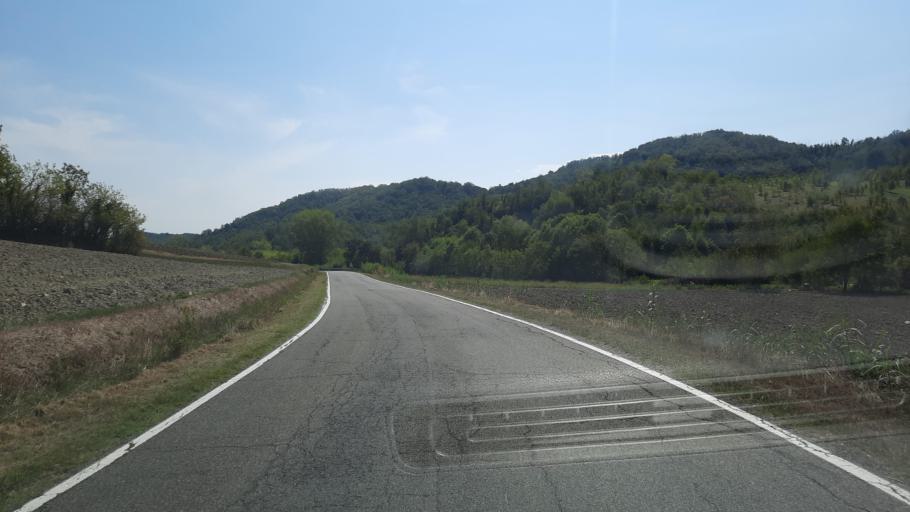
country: IT
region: Piedmont
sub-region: Provincia di Alessandria
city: Mombello Monferrato
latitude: 45.1532
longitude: 8.2595
